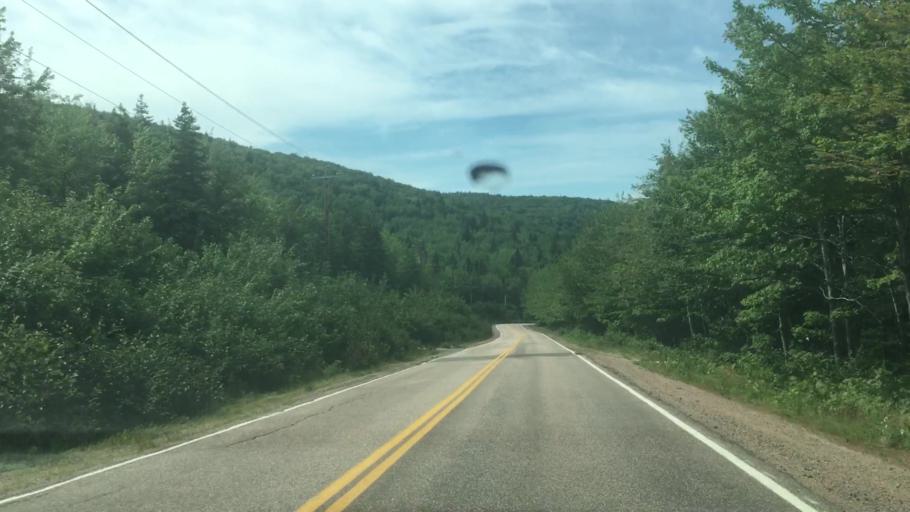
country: CA
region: Nova Scotia
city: Sydney Mines
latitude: 46.6060
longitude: -60.3938
